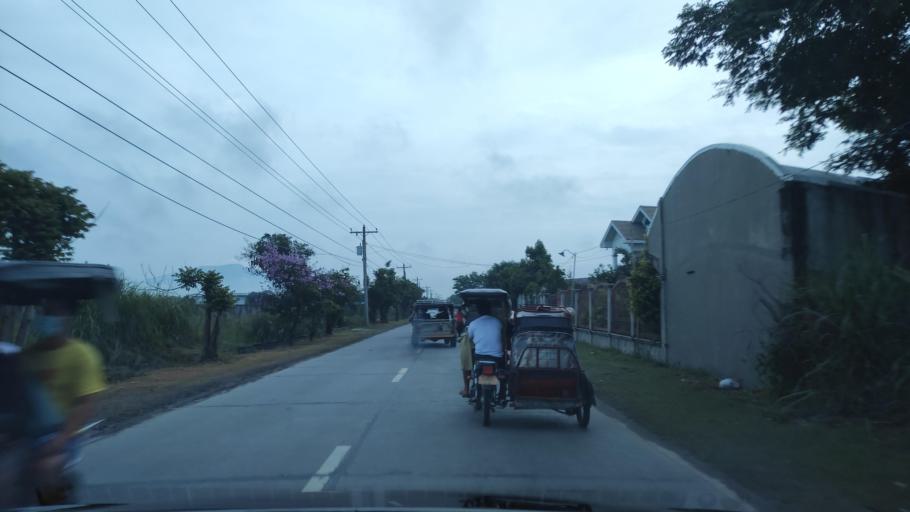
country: PH
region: Central Luzon
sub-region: Province of Pampanga
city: Santo Domingo
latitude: 15.0644
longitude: 120.7553
